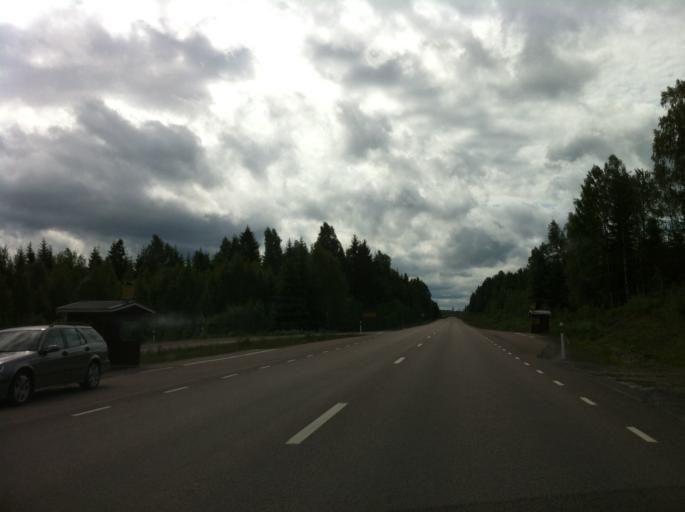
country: SE
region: Vaermland
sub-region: Sunne Kommun
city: Sunne
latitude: 59.7607
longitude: 13.1135
